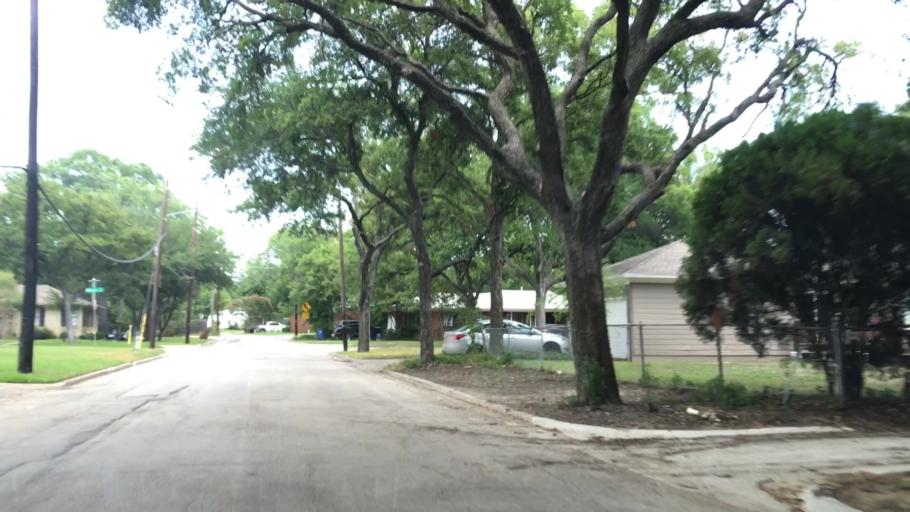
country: US
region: Texas
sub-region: Dallas County
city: University Park
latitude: 32.8749
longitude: -96.8530
